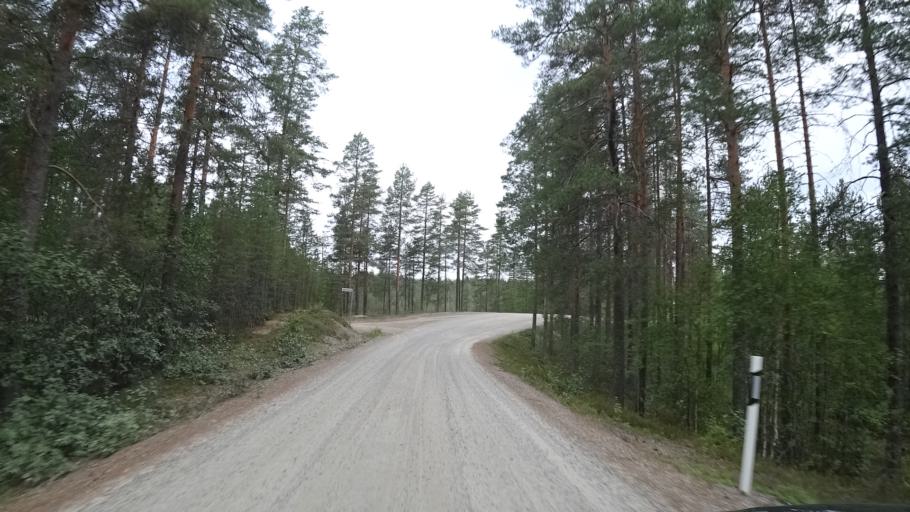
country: FI
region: North Karelia
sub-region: Pielisen Karjala
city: Lieksa
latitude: 63.2557
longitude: 30.3217
